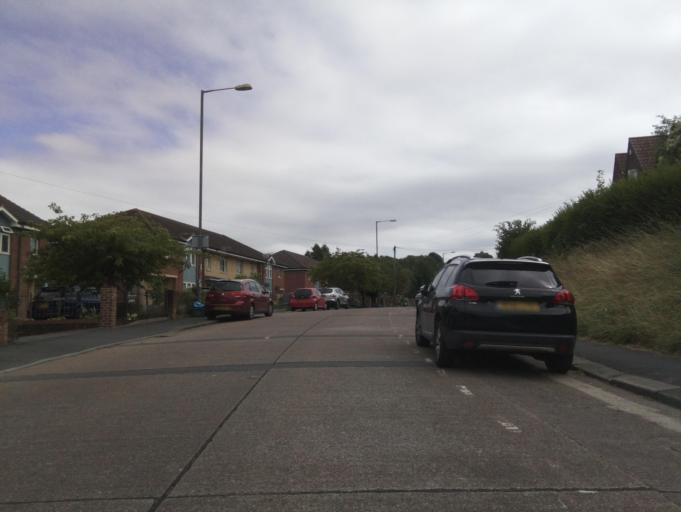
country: GB
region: England
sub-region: Bristol
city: Bristol
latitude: 51.4331
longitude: -2.5865
